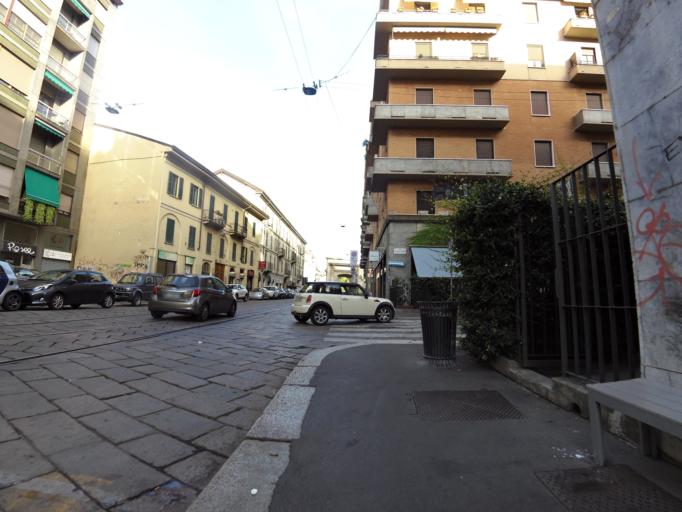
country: IT
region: Lombardy
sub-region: Citta metropolitana di Milano
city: Milano
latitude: 45.4531
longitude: 9.2006
